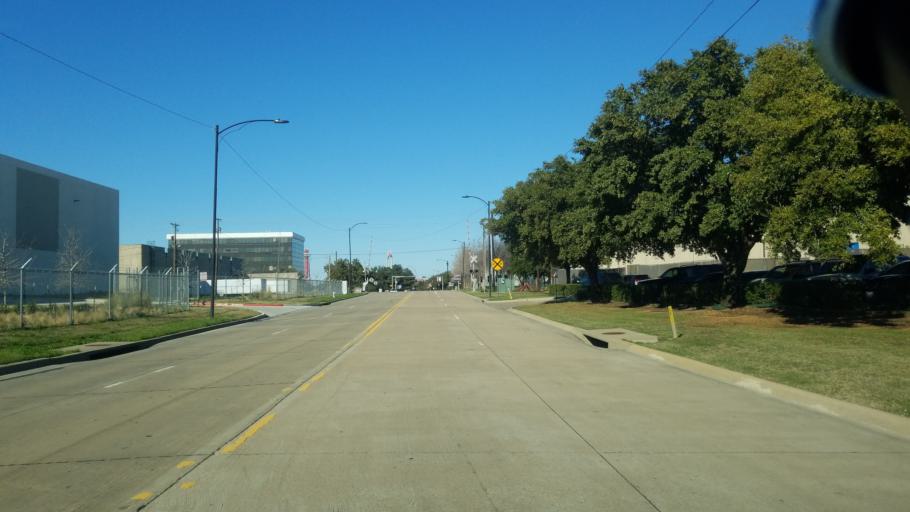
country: US
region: Texas
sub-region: Tarrant County
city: Arlington
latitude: 32.7457
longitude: -97.0688
